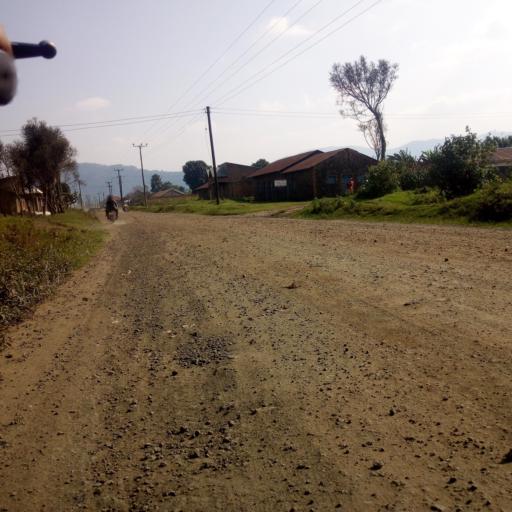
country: UG
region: Western Region
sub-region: Kisoro District
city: Kisoro
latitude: -1.2388
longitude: 29.7137
